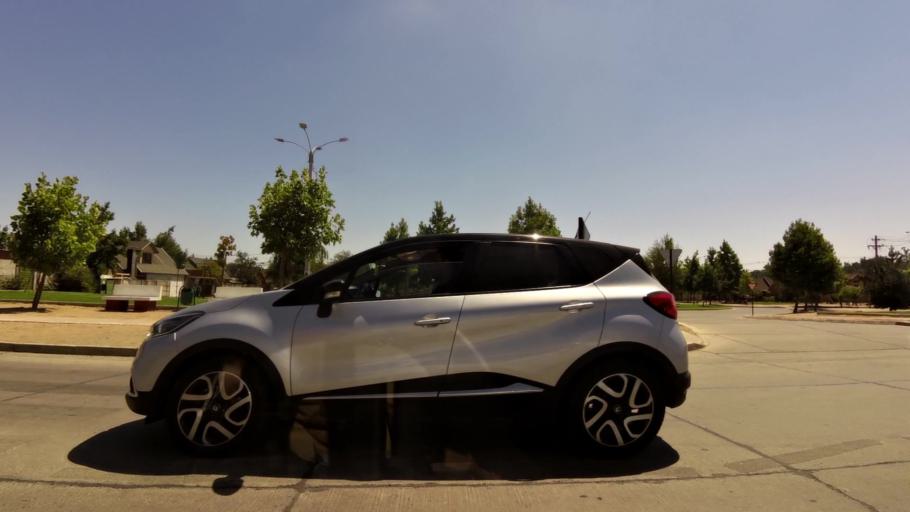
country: CL
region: Maule
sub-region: Provincia de Talca
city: Talca
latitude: -35.4280
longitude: -71.6195
